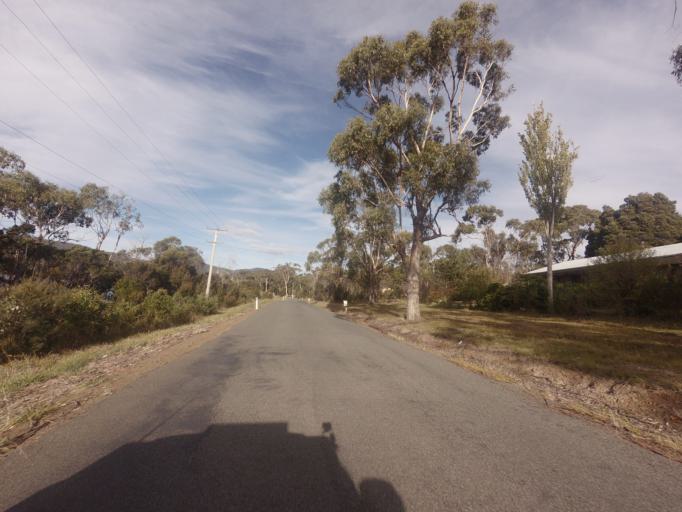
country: AU
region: Tasmania
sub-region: Sorell
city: Sorell
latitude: -42.9465
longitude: 147.8608
